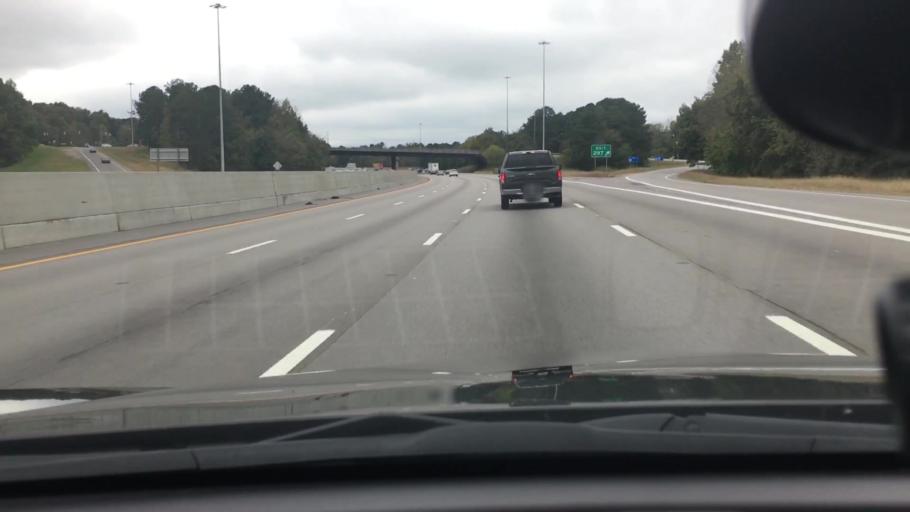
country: US
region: North Carolina
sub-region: Wake County
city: Raleigh
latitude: 35.7570
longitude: -78.6613
